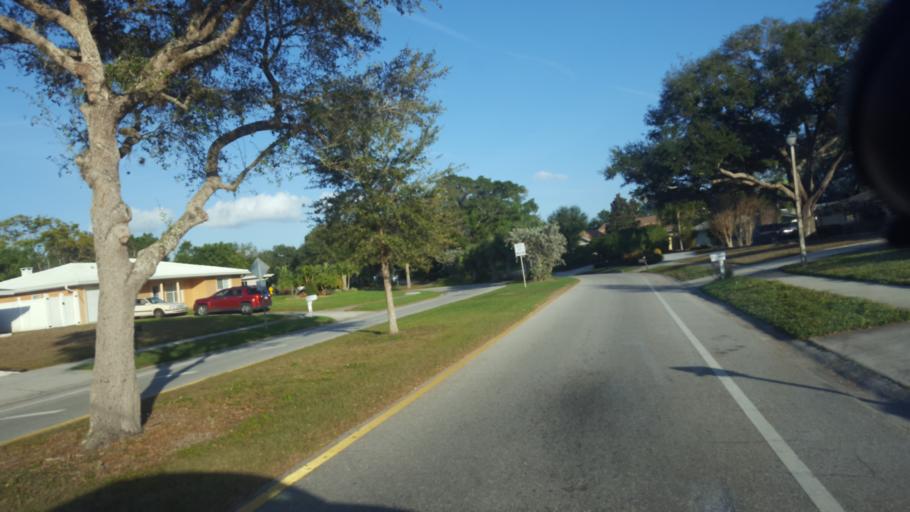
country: US
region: Florida
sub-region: Sarasota County
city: Southgate
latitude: 27.3030
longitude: -82.5213
